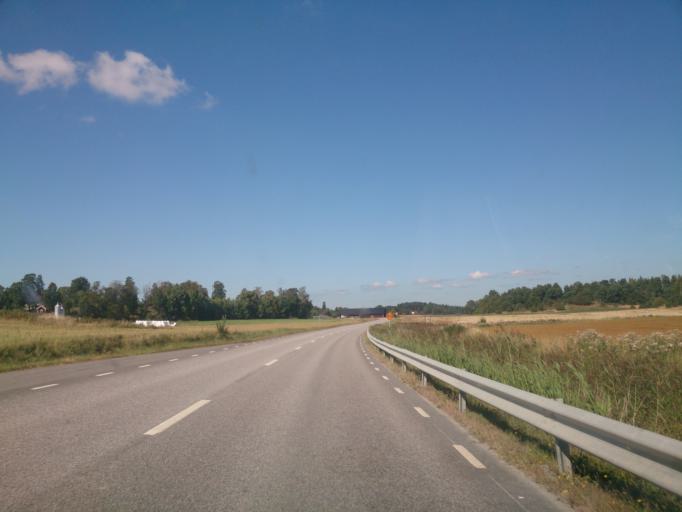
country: SE
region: OEstergoetland
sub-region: Norrkopings Kommun
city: Krokek
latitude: 58.5725
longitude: 16.5818
